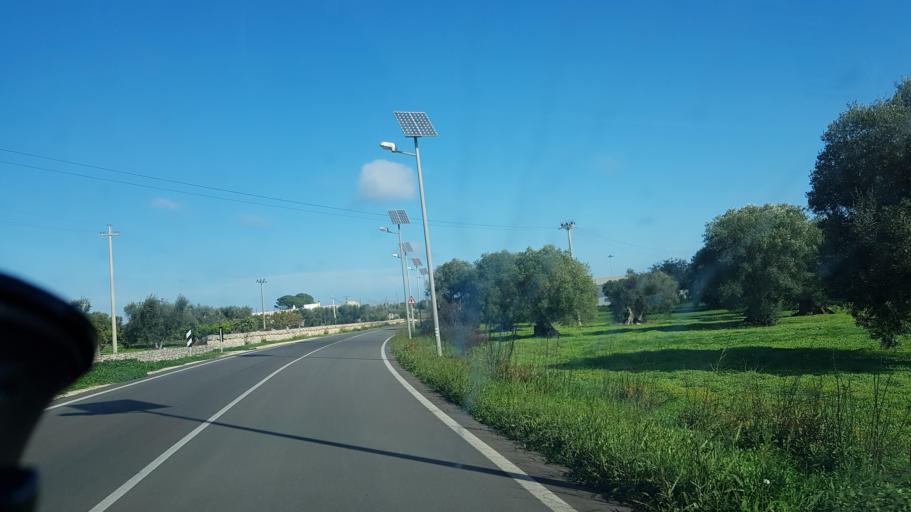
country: IT
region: Apulia
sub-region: Provincia di Brindisi
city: San Vito dei Normanni
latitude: 40.6689
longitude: 17.7054
